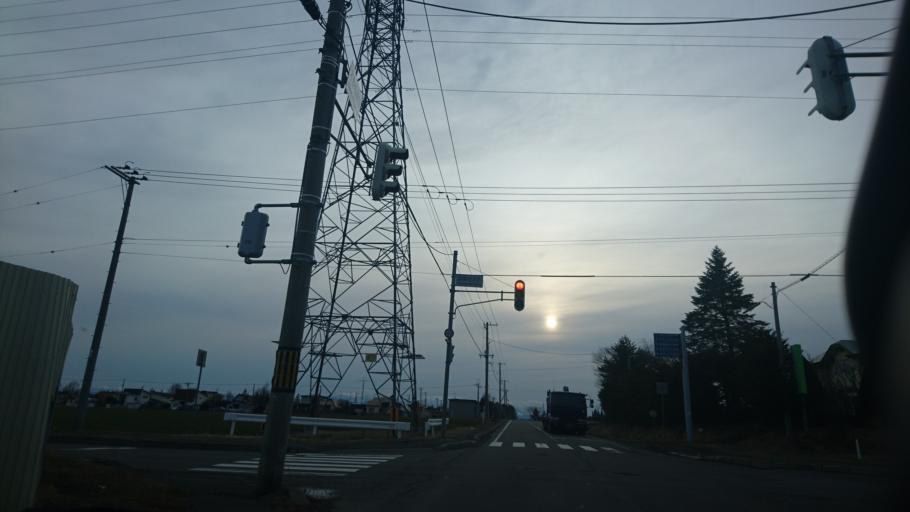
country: JP
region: Hokkaido
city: Otofuke
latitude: 42.9768
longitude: 143.1983
